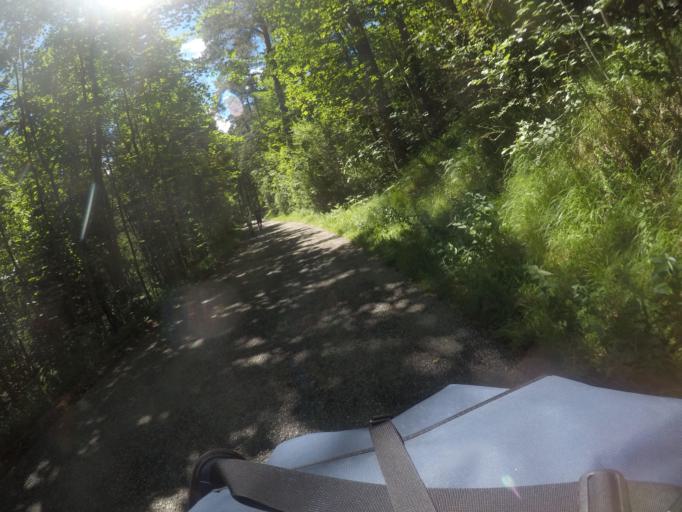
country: AT
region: Tyrol
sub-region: Politischer Bezirk Reutte
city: Musau
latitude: 47.5627
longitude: 10.6670
